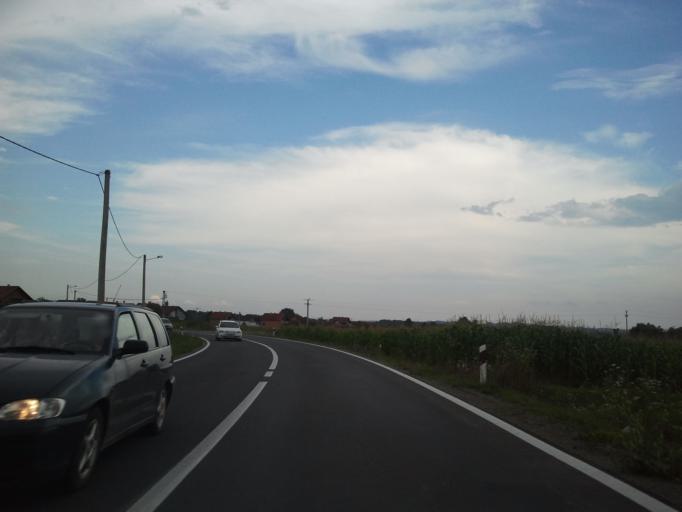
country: HR
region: Sisacko-Moslavacka
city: Glina
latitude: 45.3417
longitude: 16.0573
